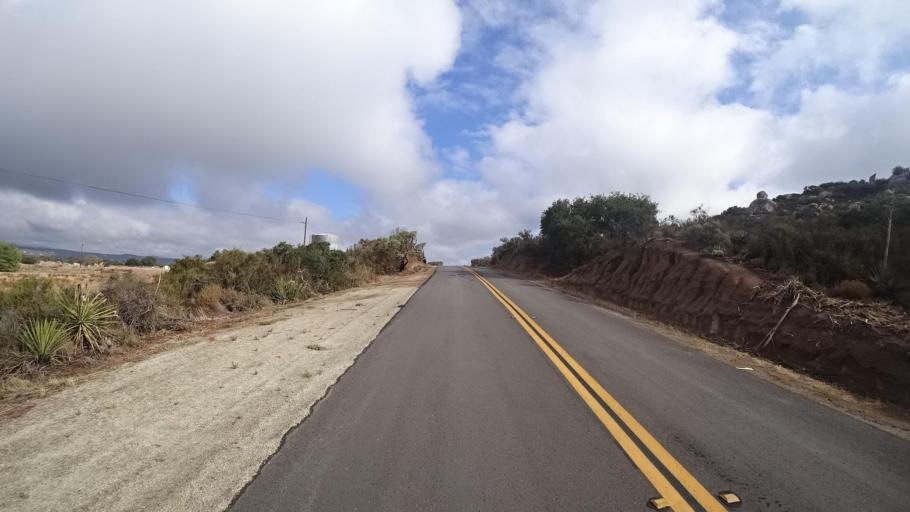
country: MX
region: Baja California
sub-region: Tecate
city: Hacienda Tecate
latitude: 32.6127
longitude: -116.5696
